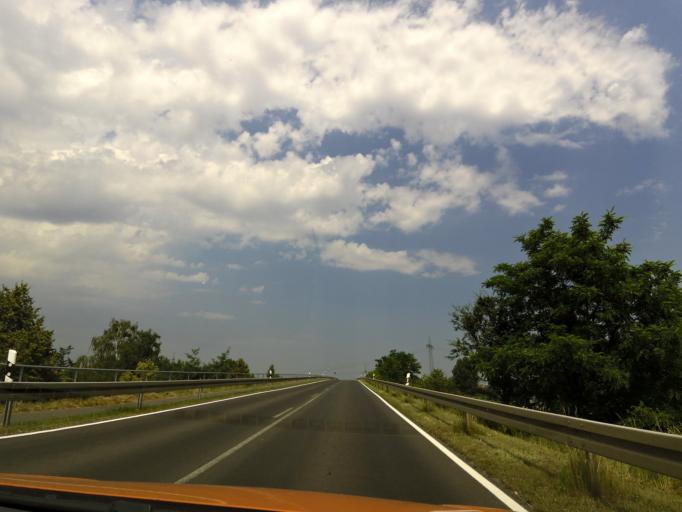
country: DE
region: Brandenburg
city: Wustermark
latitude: 52.5504
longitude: 12.9378
